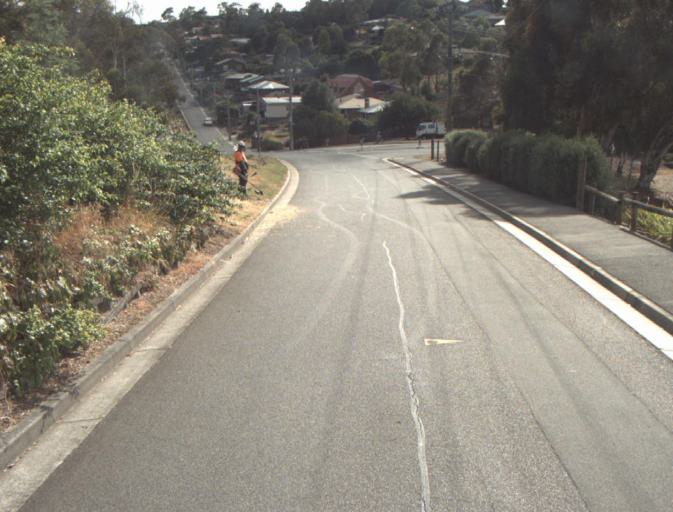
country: AU
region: Tasmania
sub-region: Launceston
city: Summerhill
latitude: -41.4637
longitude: 147.1221
